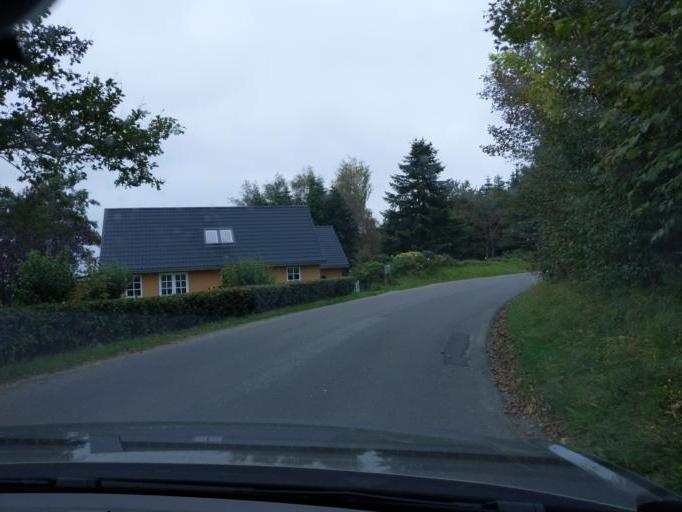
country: DK
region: Central Jutland
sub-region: Viborg Kommune
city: Stoholm
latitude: 56.4814
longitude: 9.2289
